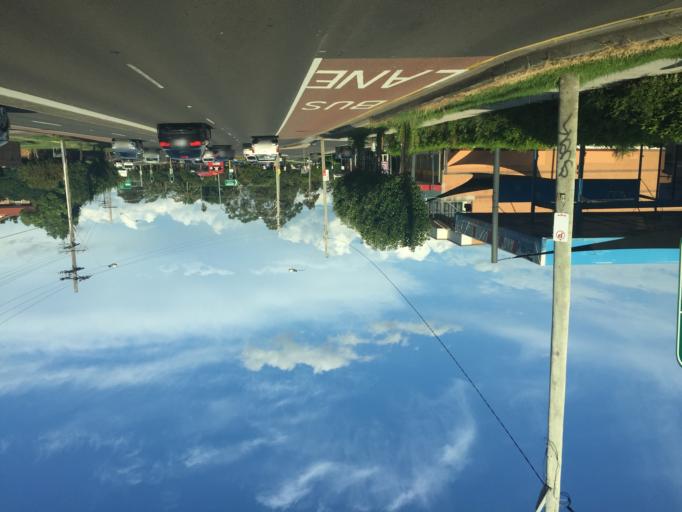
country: AU
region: New South Wales
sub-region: Parramatta
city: Paramatta
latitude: -33.8085
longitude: 151.0175
